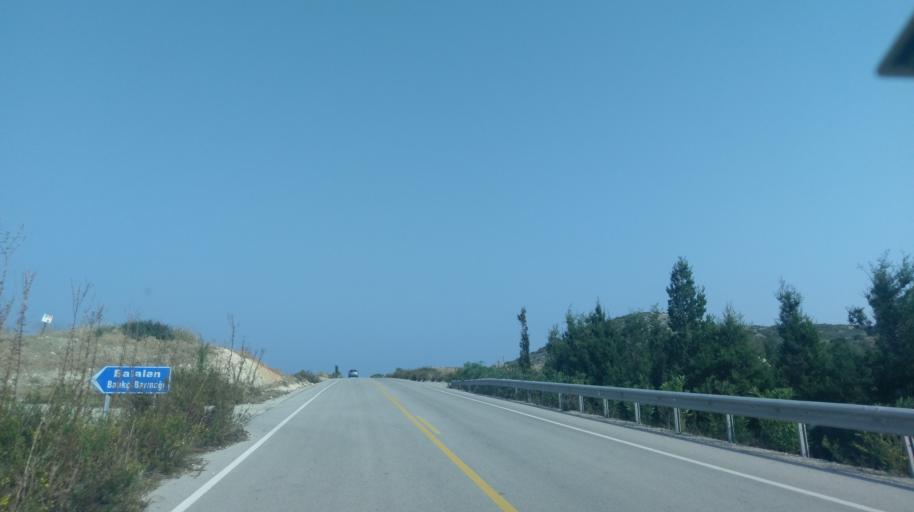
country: CY
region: Ammochostos
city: Leonarisso
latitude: 35.4887
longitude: 34.0790
